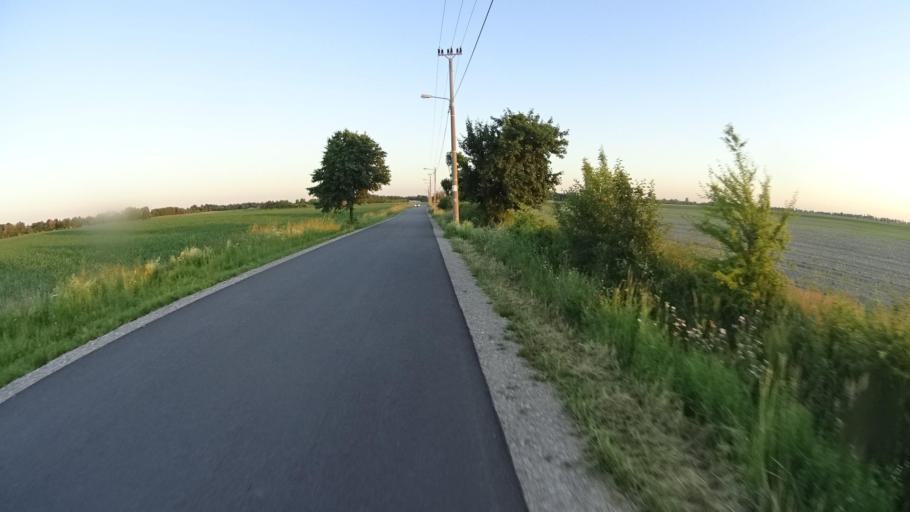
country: PL
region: Masovian Voivodeship
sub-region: Powiat warszawski zachodni
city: Jozefow
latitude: 52.2566
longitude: 20.6756
